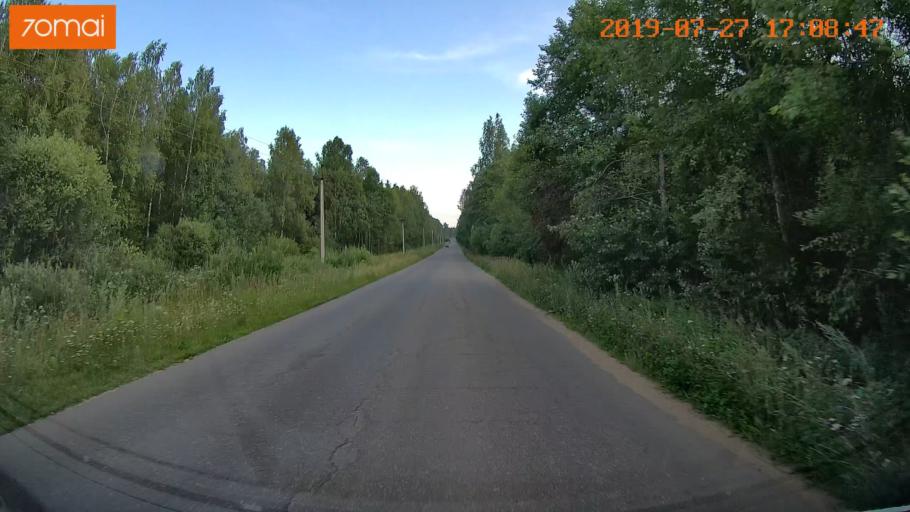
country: RU
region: Ivanovo
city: Novo-Talitsy
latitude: 57.0798
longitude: 40.8414
